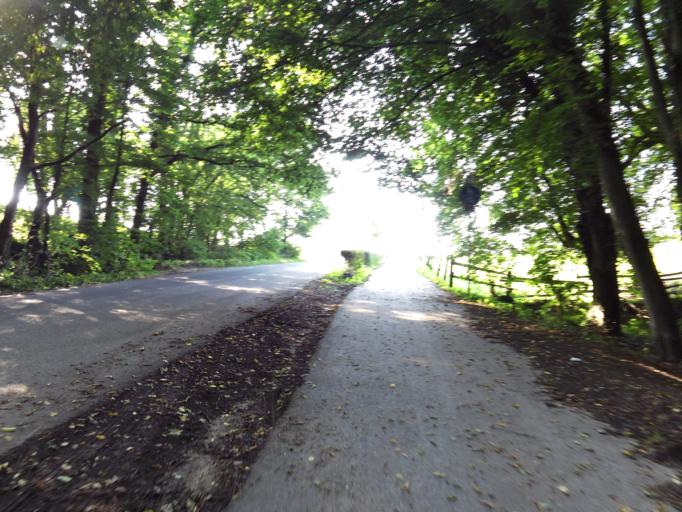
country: DE
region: North Rhine-Westphalia
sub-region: Regierungsbezirk Koln
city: Herzogenrath
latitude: 50.9043
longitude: 6.0895
